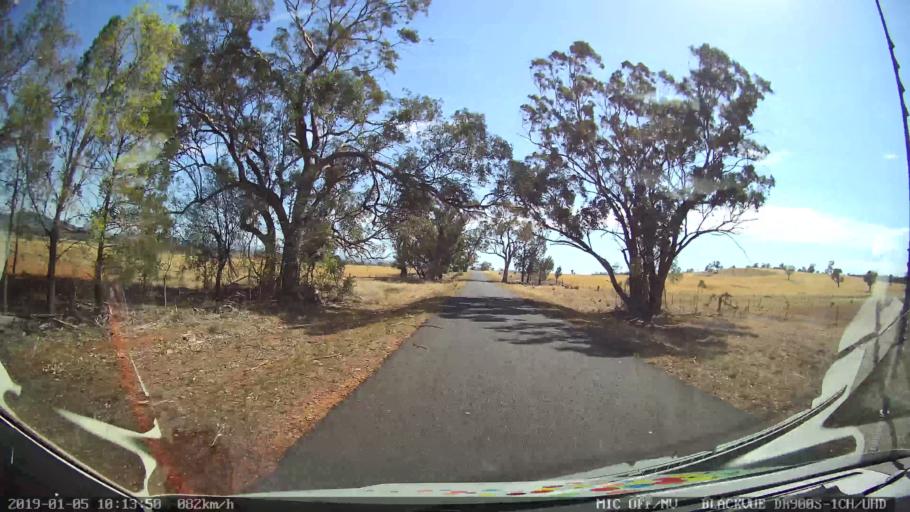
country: AU
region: New South Wales
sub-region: Gilgandra
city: Gilgandra
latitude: -31.5985
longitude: 148.9286
